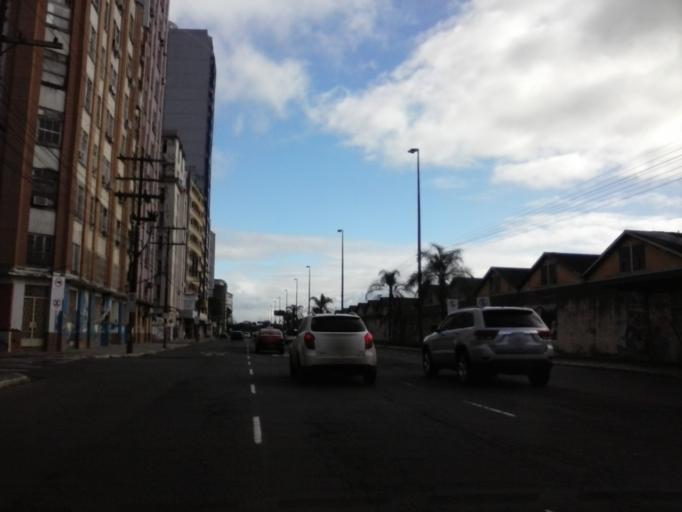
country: BR
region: Rio Grande do Sul
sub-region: Porto Alegre
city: Porto Alegre
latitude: -30.0281
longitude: -51.2323
